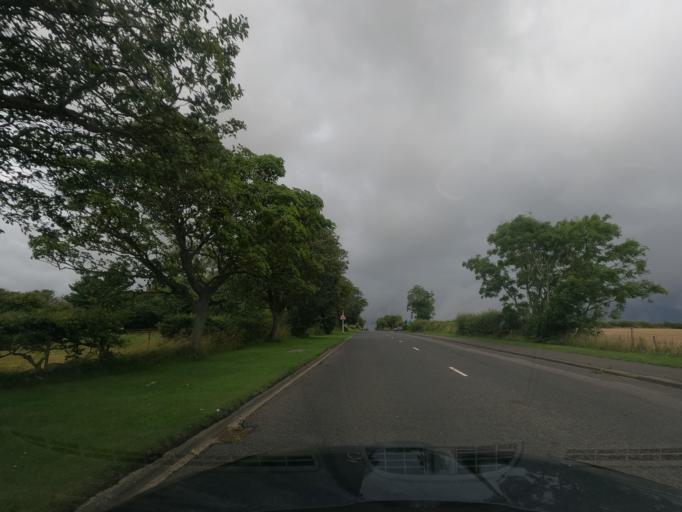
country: GB
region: England
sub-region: Northumberland
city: Berwick-Upon-Tweed
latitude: 55.7473
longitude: -1.9990
